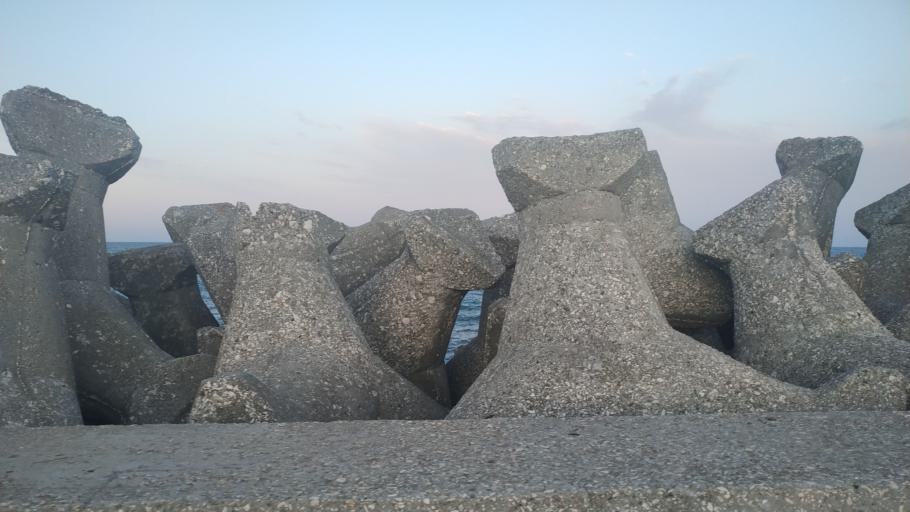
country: RO
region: Constanta
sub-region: Municipiul Constanta
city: Constanta
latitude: 44.1693
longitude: 28.6603
